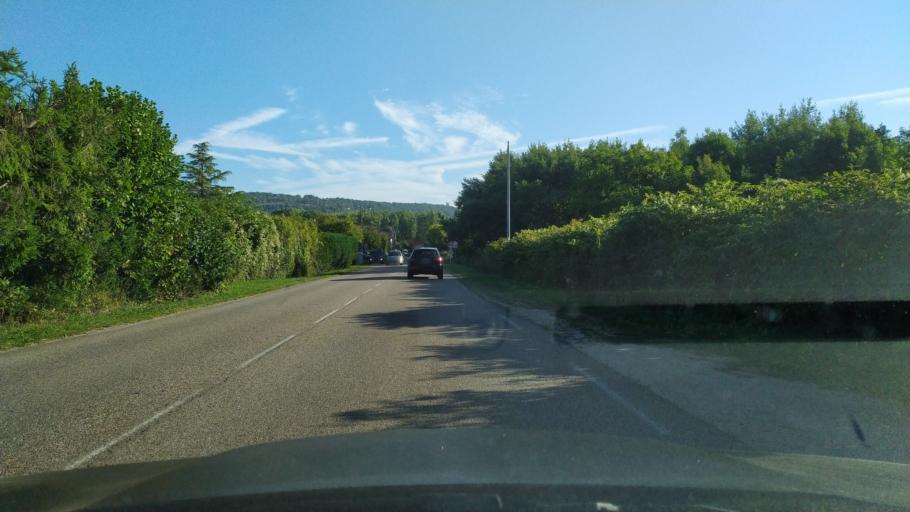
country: FR
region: Lorraine
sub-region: Departement de la Moselle
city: Moulins-les-Metz
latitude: 49.0996
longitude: 6.1065
